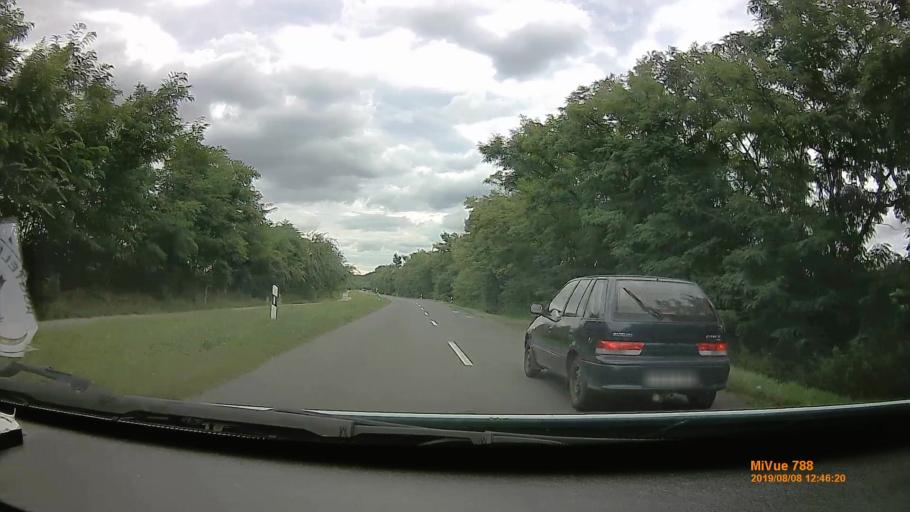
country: HU
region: Szabolcs-Szatmar-Bereg
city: Hodasz
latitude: 47.8955
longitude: 22.2179
